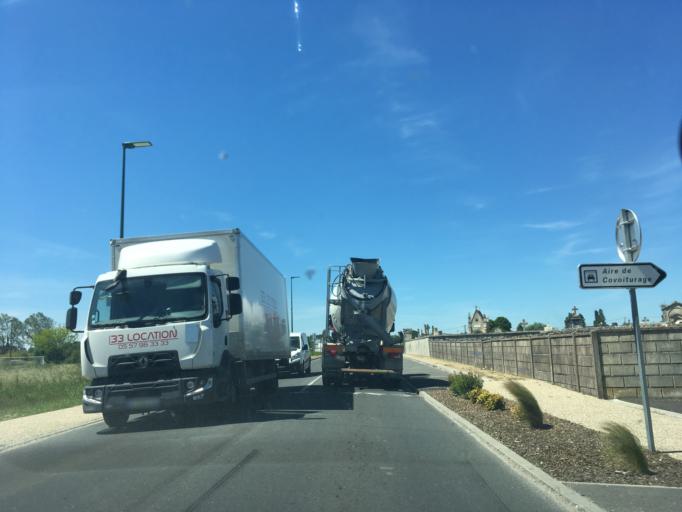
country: FR
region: Aquitaine
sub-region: Departement de la Gironde
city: Listrac-Medoc
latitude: 45.0763
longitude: -0.7933
